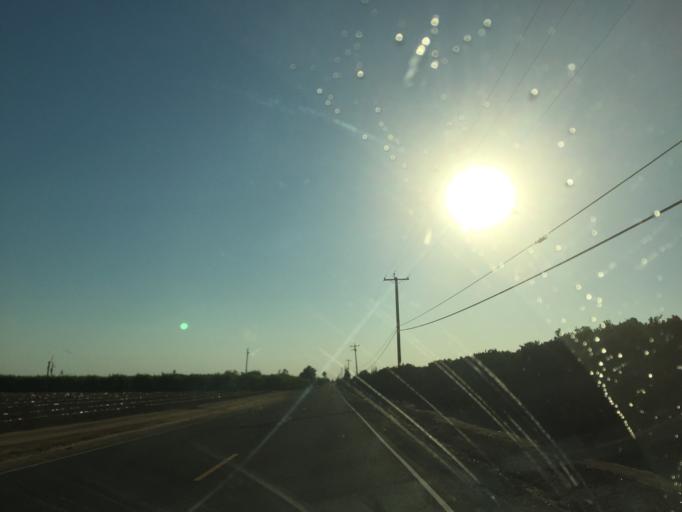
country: US
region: California
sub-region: Fresno County
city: Orange Cove
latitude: 36.6242
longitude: -119.2918
